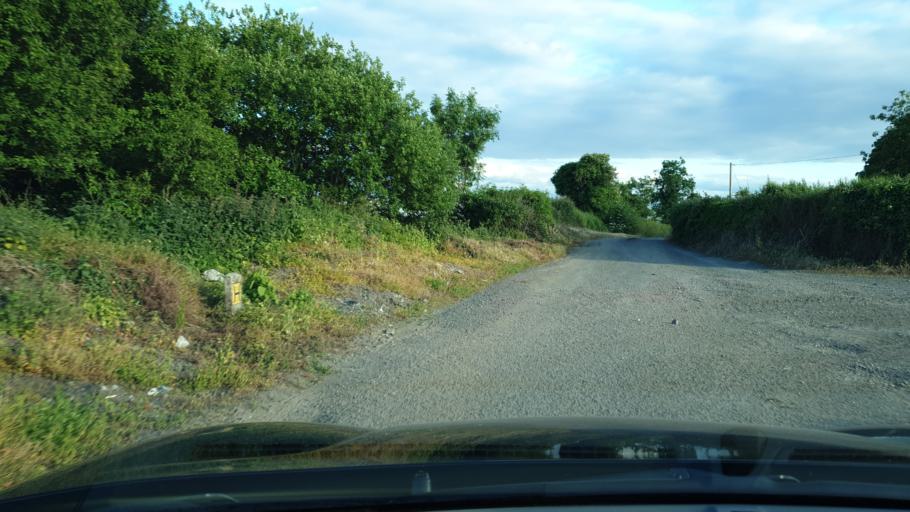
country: IE
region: Leinster
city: Hartstown
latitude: 53.4336
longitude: -6.4042
